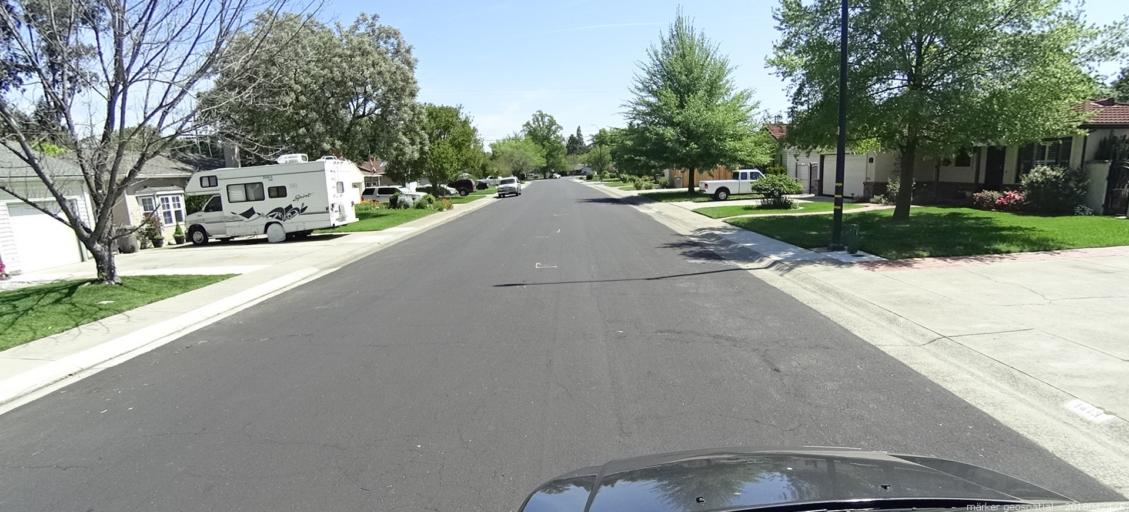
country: US
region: California
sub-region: Yolo County
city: West Sacramento
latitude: 38.5746
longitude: -121.5334
